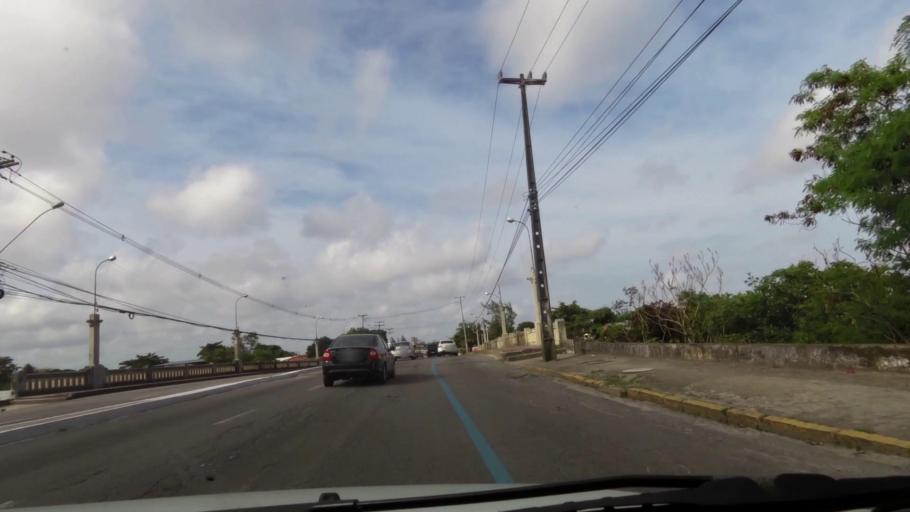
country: BR
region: Pernambuco
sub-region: Recife
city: Recife
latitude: -8.0821
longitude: -34.9056
